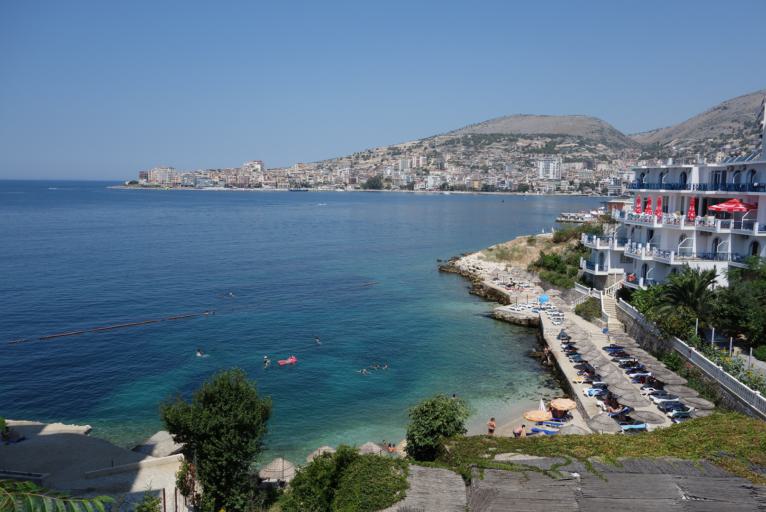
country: AL
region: Vlore
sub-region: Rrethi i Sarandes
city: Sarande
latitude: 39.8663
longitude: 20.0164
